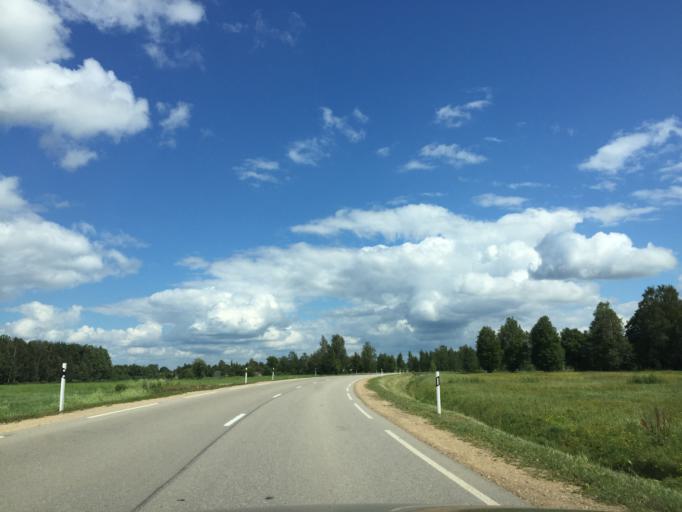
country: LV
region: Malpils
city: Malpils
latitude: 56.9000
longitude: 24.9133
